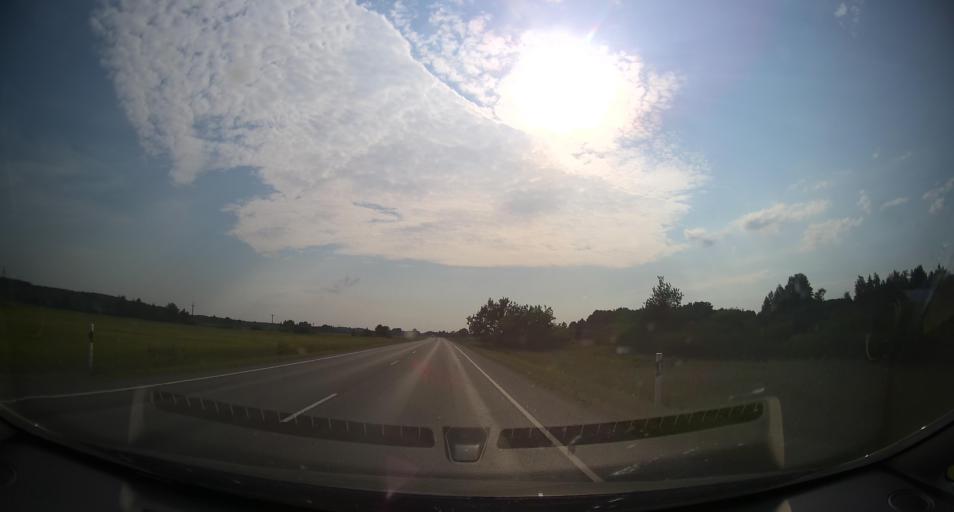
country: EE
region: Laeaene
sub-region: Lihula vald
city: Lihula
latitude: 58.7106
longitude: 23.8618
